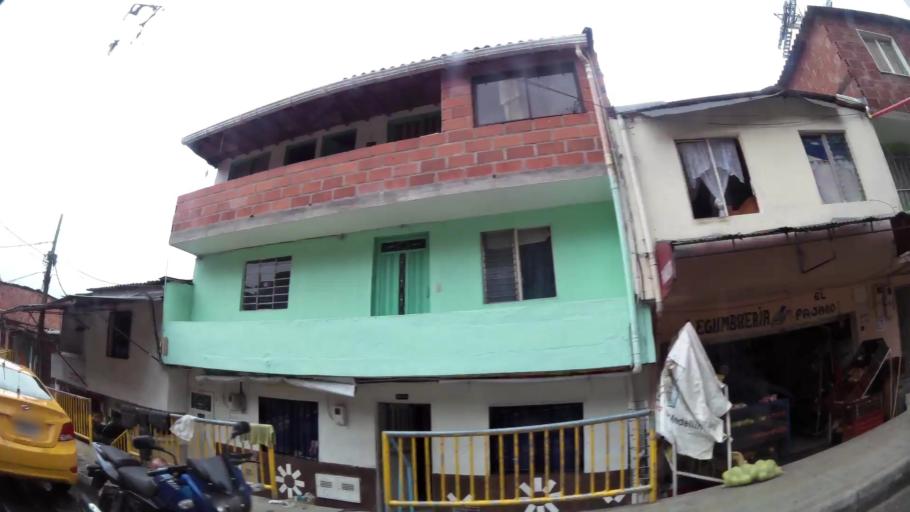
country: CO
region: Antioquia
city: Bello
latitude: 6.2962
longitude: -75.5521
